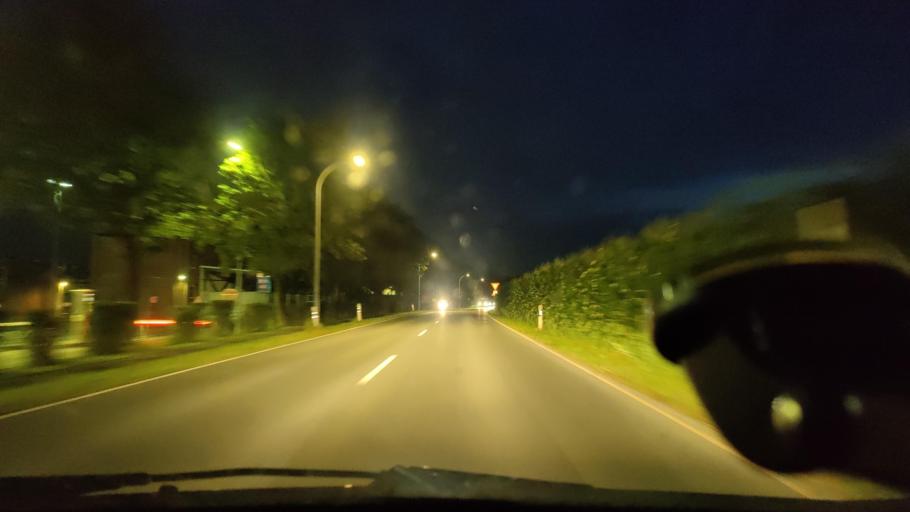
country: DE
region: North Rhine-Westphalia
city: Rheinberg
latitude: 51.5674
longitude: 6.5780
